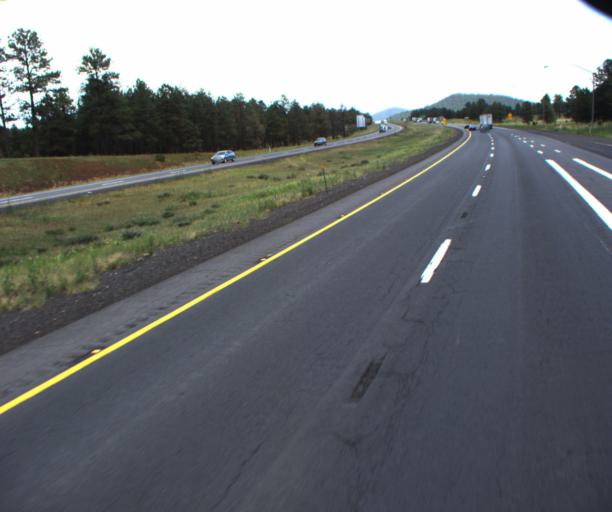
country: US
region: Arizona
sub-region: Coconino County
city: Williams
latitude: 35.2582
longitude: -112.1445
